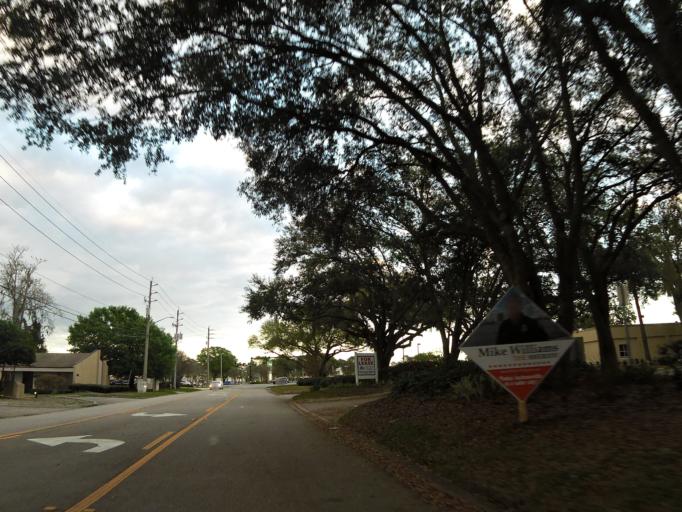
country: US
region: Florida
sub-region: Saint Johns County
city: Fruit Cove
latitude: 30.1856
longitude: -81.6298
